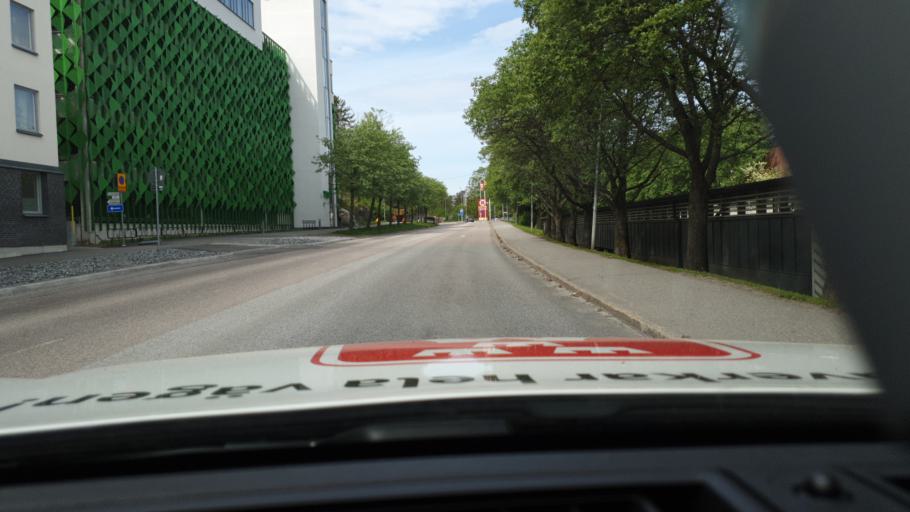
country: SE
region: Stockholm
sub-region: Tyreso Kommun
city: Bollmora
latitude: 59.2428
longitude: 18.2226
